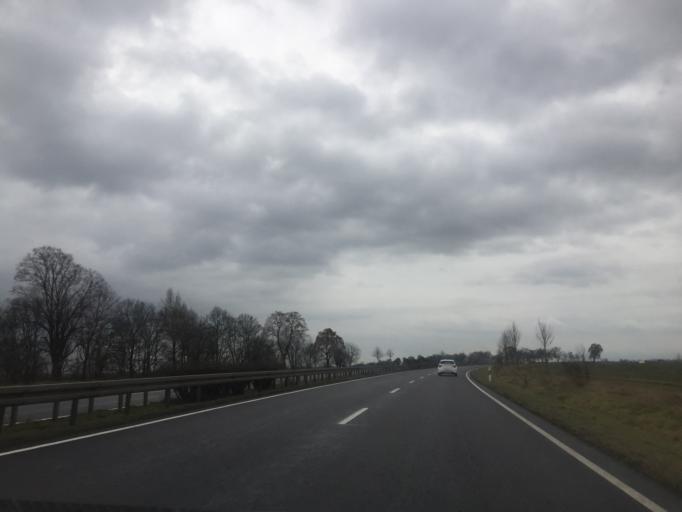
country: DE
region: Saxony-Anhalt
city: Hohendodeleben
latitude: 52.0289
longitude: 11.5175
